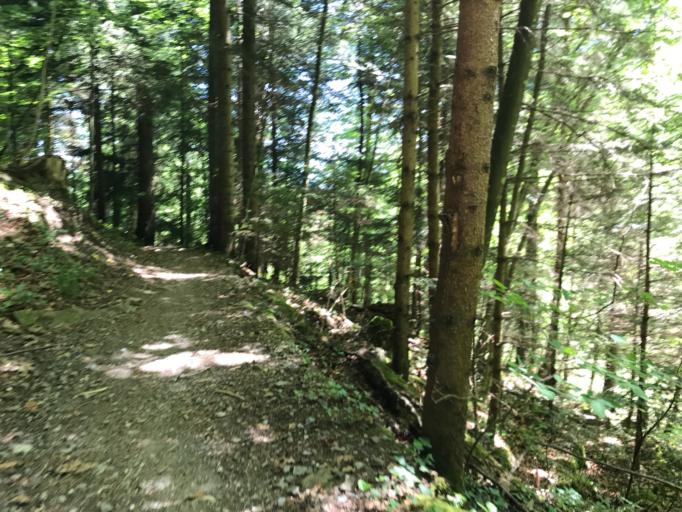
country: CH
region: Nidwalden
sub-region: Nidwalden
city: Hergiswil
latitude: 46.9882
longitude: 8.2913
